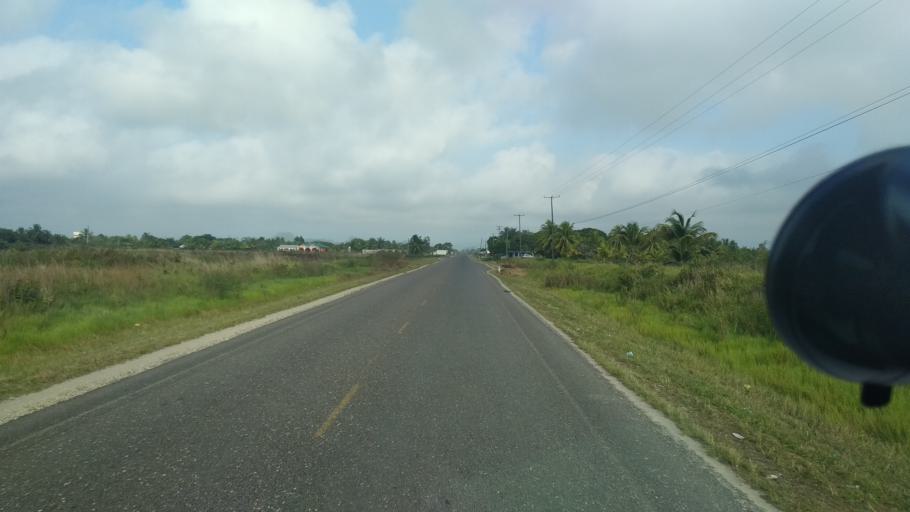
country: BZ
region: Stann Creek
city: Placencia
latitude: 16.5109
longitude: -88.5401
